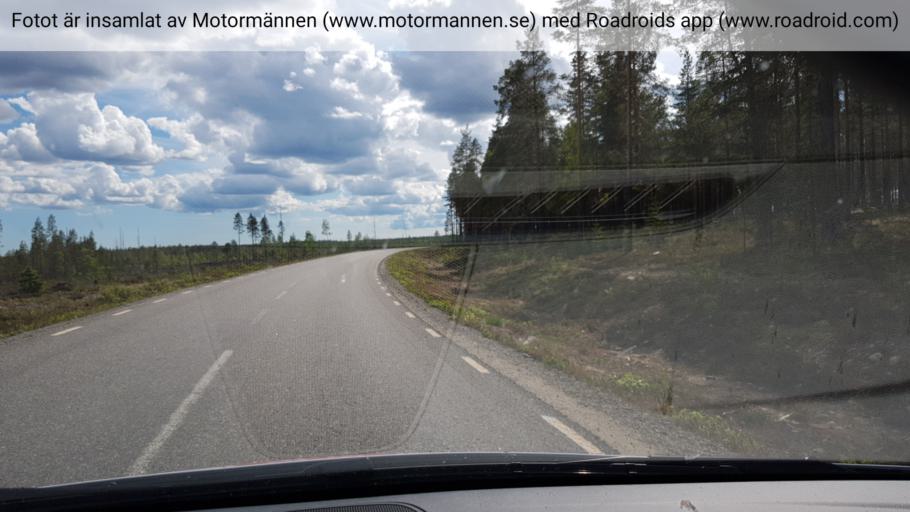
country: SE
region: Vaesterbotten
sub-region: Umea Kommun
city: Ersmark
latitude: 64.1919
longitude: 20.3370
